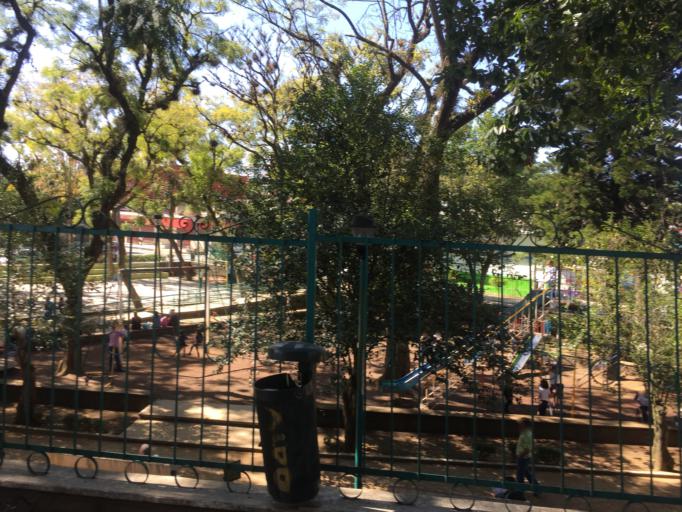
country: MX
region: Veracruz
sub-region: Xalapa
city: Xalapa de Enriquez
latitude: 19.5286
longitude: -96.9060
